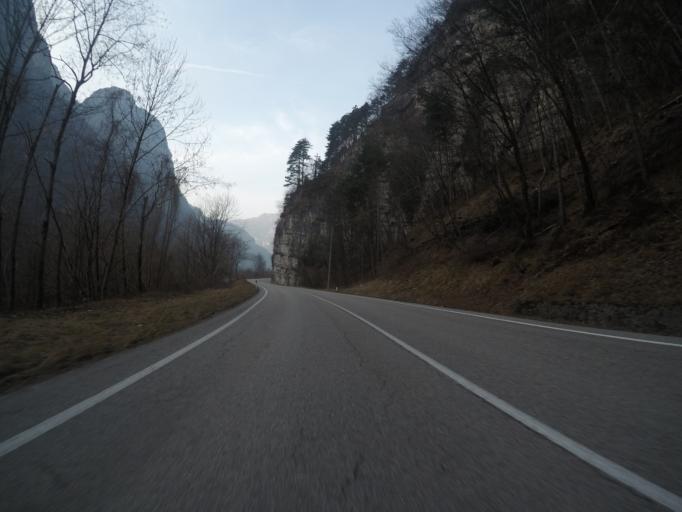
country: IT
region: Veneto
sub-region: Provincia di Belluno
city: La Valle Agordina
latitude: 46.2258
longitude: 12.1180
